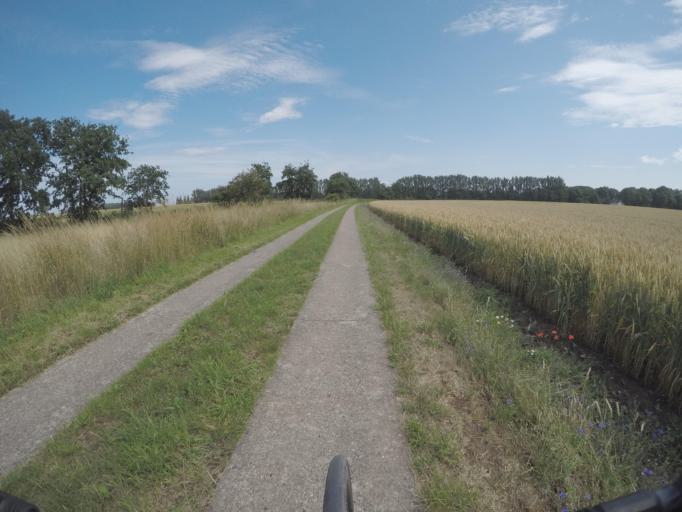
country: DE
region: Mecklenburg-Vorpommern
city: Altefahr
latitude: 54.3674
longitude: 13.1438
